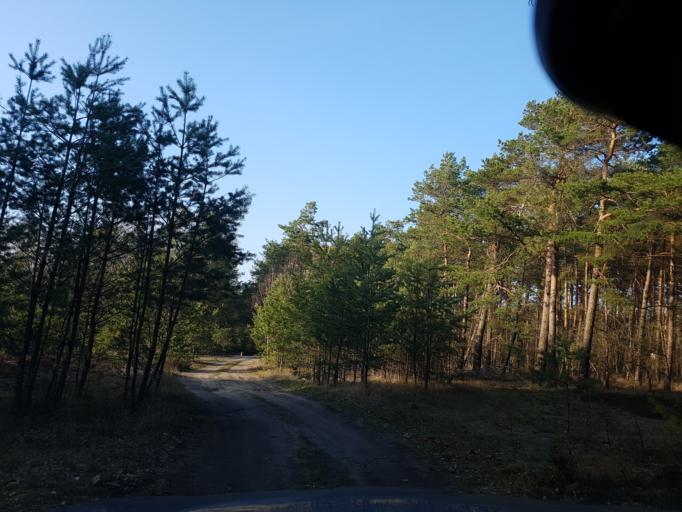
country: DE
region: Brandenburg
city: Schonewalde
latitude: 51.6351
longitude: 13.6156
